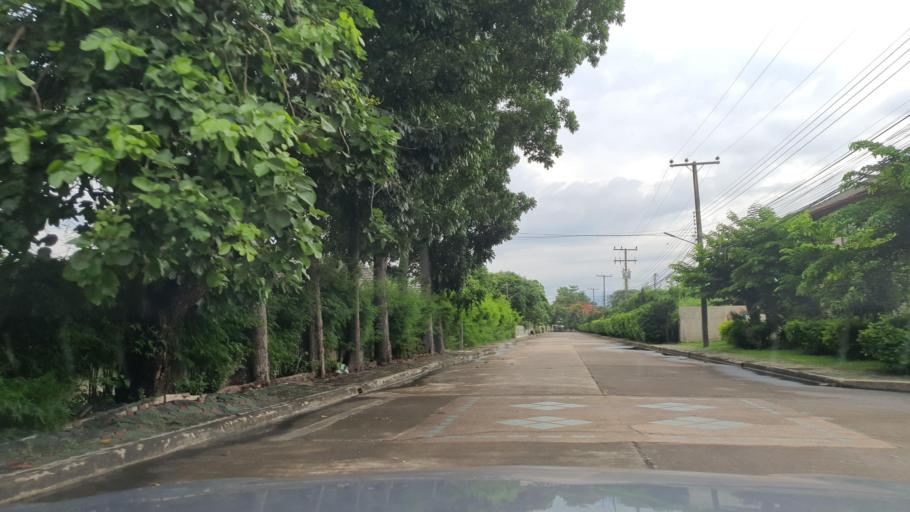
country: TH
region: Chiang Mai
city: San Kamphaeng
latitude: 18.7752
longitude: 99.0712
